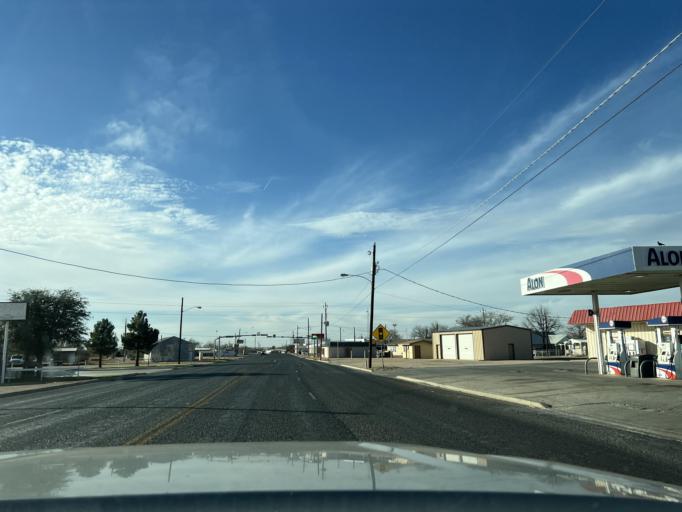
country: US
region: Texas
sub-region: Scurry County
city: Snyder
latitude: 32.7155
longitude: -100.9003
